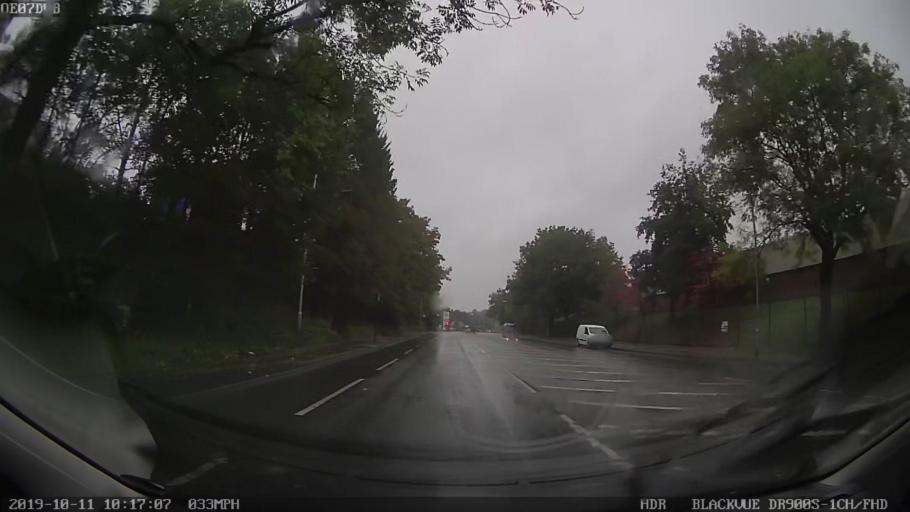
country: GB
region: England
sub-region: Borough of Rochdale
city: Middleton
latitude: 53.5375
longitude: -2.1753
